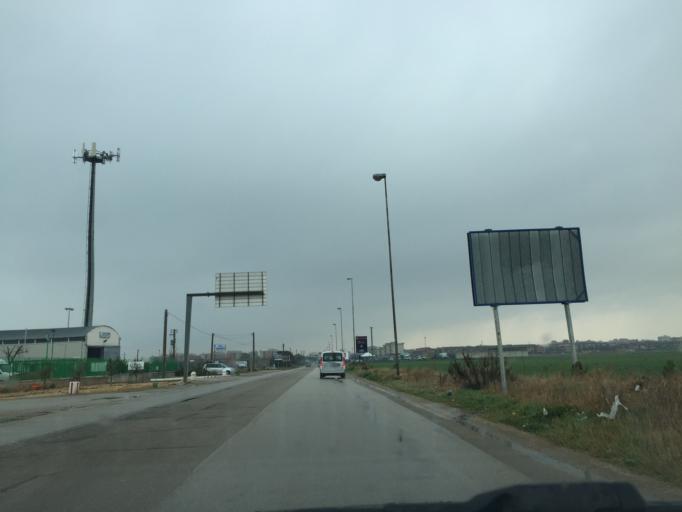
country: IT
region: Apulia
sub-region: Provincia di Foggia
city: Foggia
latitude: 41.4705
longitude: 15.5129
